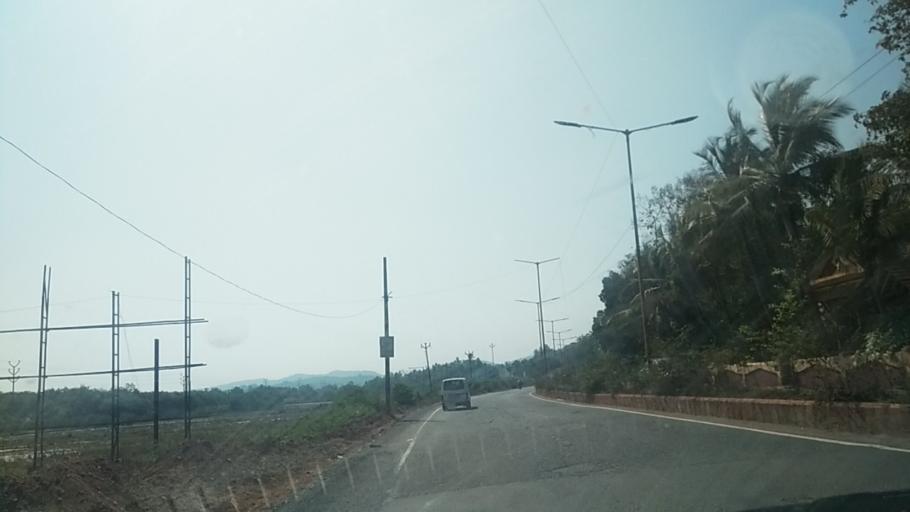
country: IN
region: Goa
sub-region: South Goa
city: Raia
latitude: 15.3305
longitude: 73.9908
